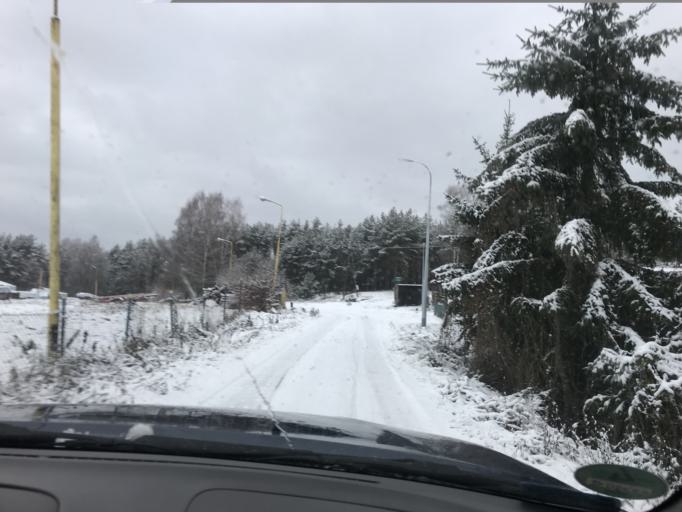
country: PL
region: Pomeranian Voivodeship
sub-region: Powiat bytowski
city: Parchowo
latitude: 54.2532
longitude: 17.5897
